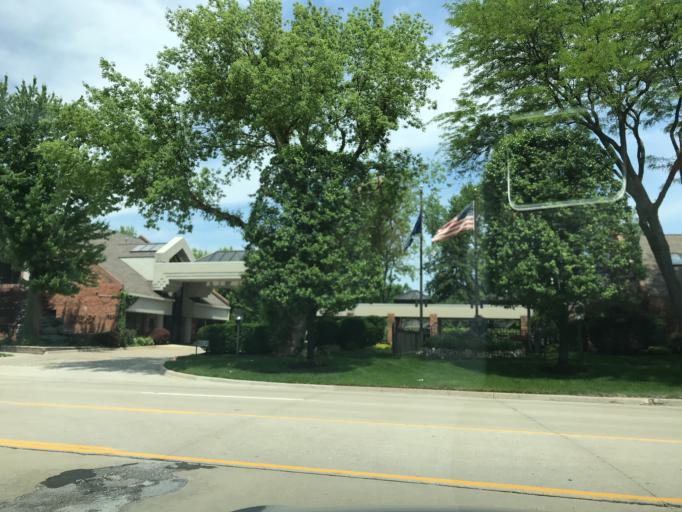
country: US
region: Michigan
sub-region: Oakland County
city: Southfield
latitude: 42.4730
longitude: -83.2347
